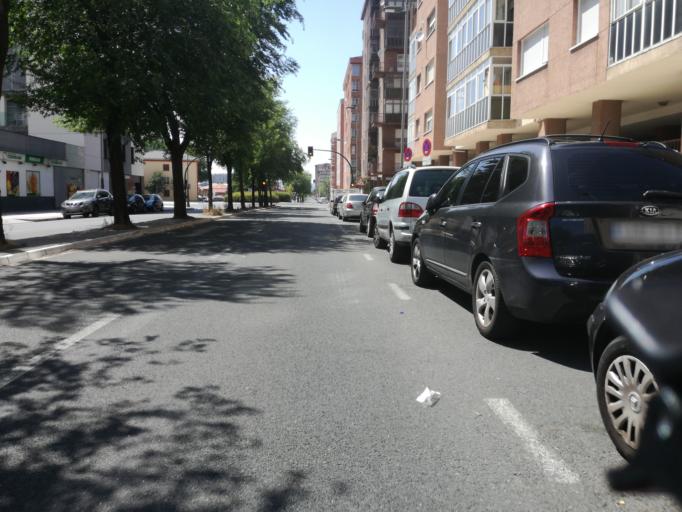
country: ES
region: Basque Country
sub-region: Provincia de Alava
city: Gasteiz / Vitoria
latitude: 42.8532
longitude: -2.6971
